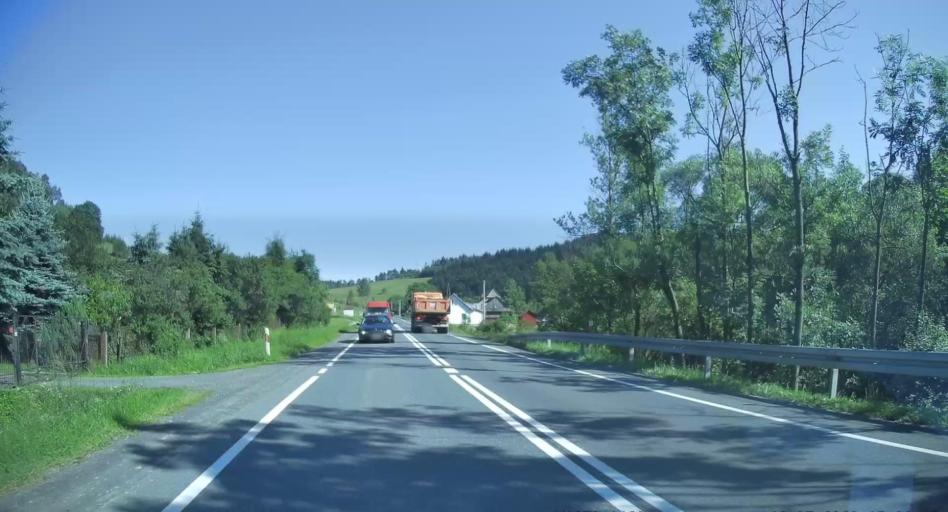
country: PL
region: Lesser Poland Voivodeship
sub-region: Powiat nowosadecki
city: Krynica-Zdroj
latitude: 49.4819
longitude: 20.9188
